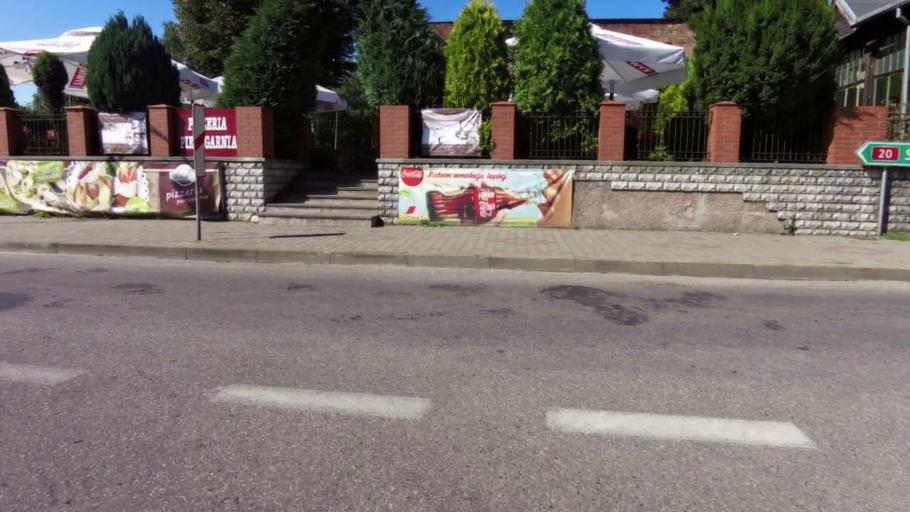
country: PL
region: West Pomeranian Voivodeship
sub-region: Powiat drawski
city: Zlocieniec
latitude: 53.5294
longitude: 16.0118
